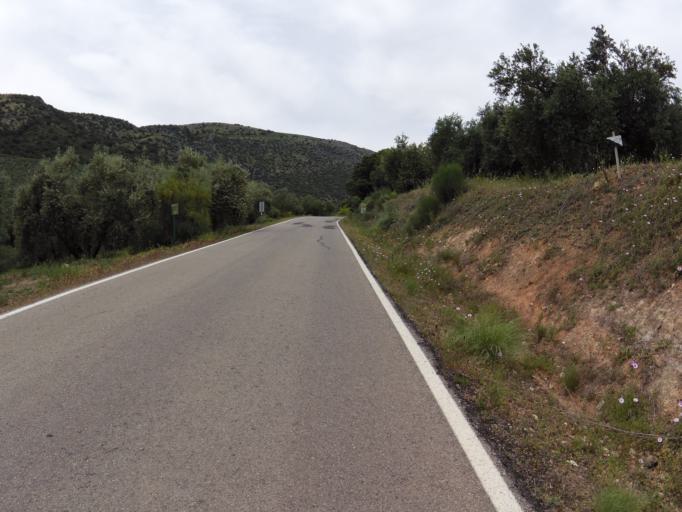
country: ES
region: Andalusia
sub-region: Province of Cordoba
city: Fuente-Tojar
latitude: 37.5181
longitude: -4.2142
